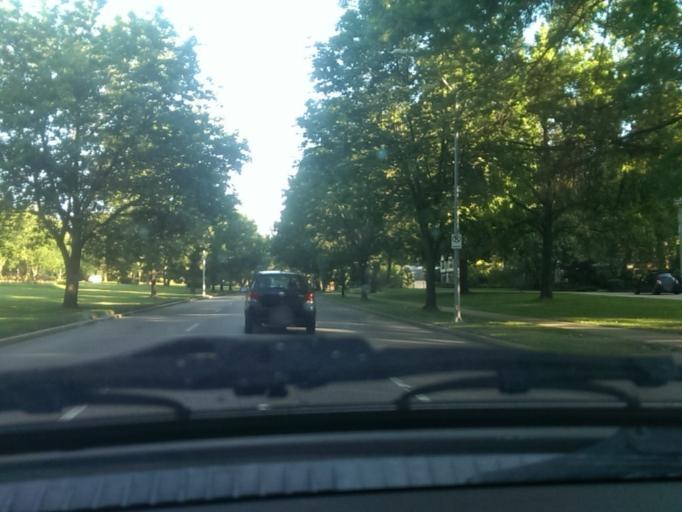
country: US
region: Kansas
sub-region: Johnson County
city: Mission Hills
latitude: 39.0237
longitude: -94.6024
